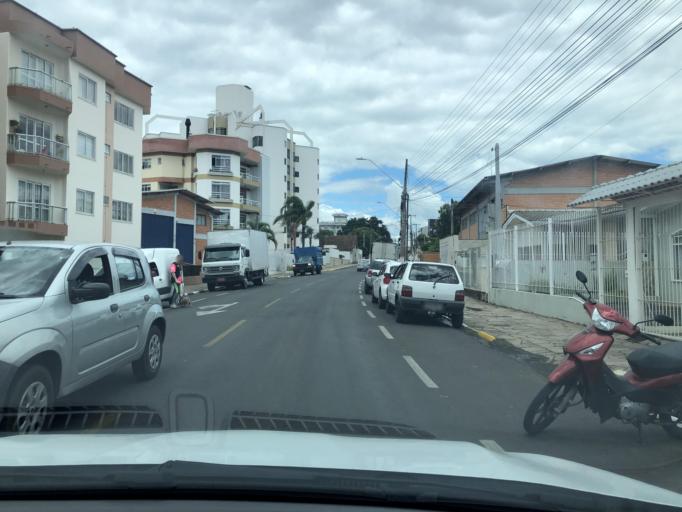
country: BR
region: Santa Catarina
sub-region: Lages
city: Lages
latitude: -27.8225
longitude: -50.3264
